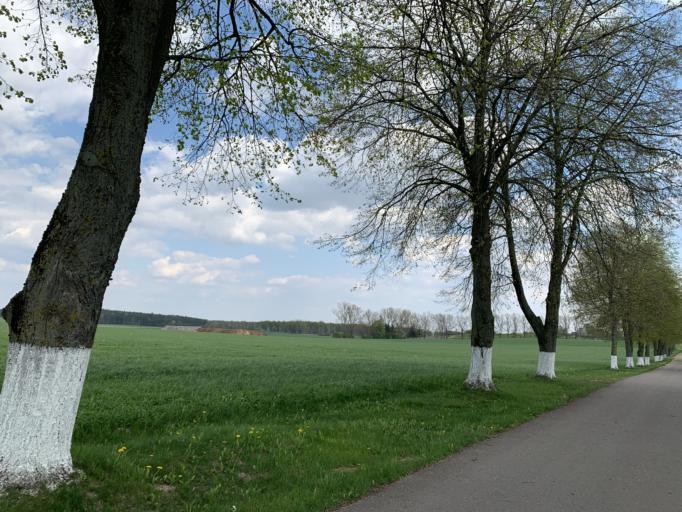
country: BY
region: Minsk
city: Nyasvizh
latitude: 53.2464
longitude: 26.6877
